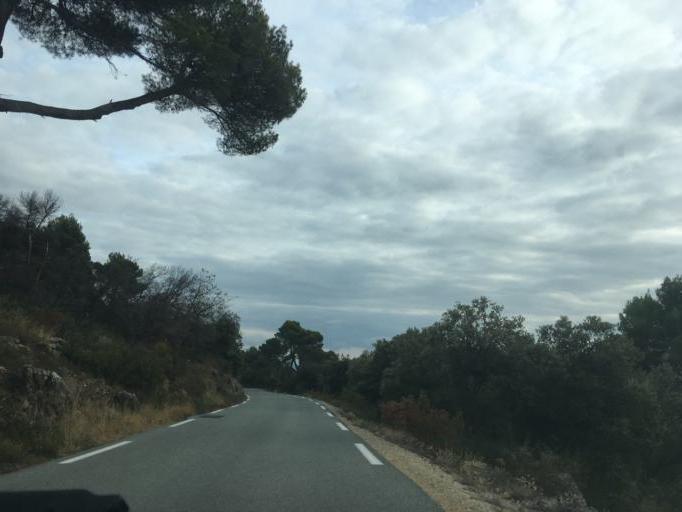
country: FR
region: Provence-Alpes-Cote d'Azur
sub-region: Departement du Var
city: Villecroze
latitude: 43.5805
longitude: 6.3110
